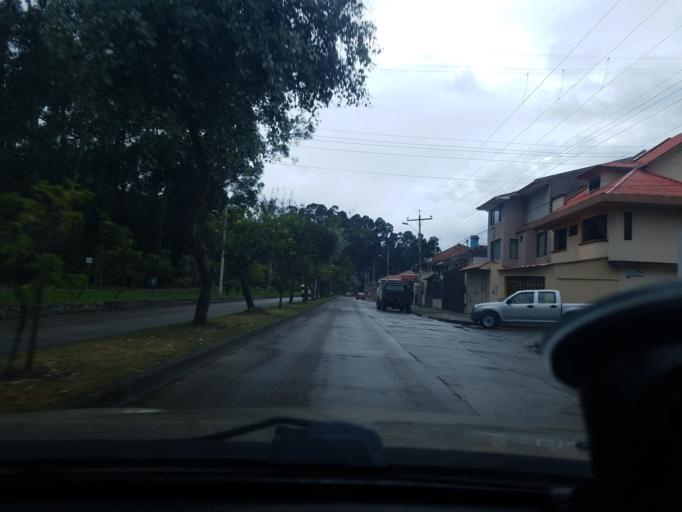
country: EC
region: Azuay
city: Cuenca
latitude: -2.9032
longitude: -78.9807
